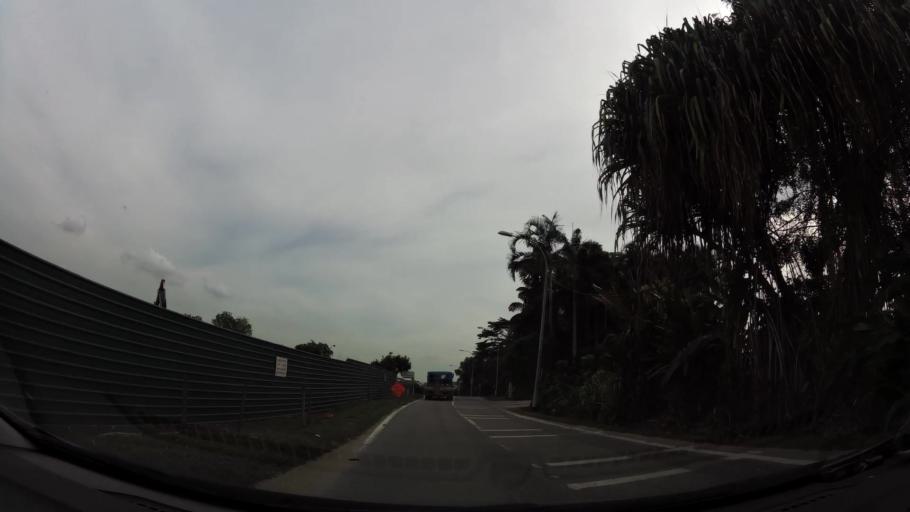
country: MY
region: Johor
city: Johor Bahru
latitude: 1.4266
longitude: 103.7208
